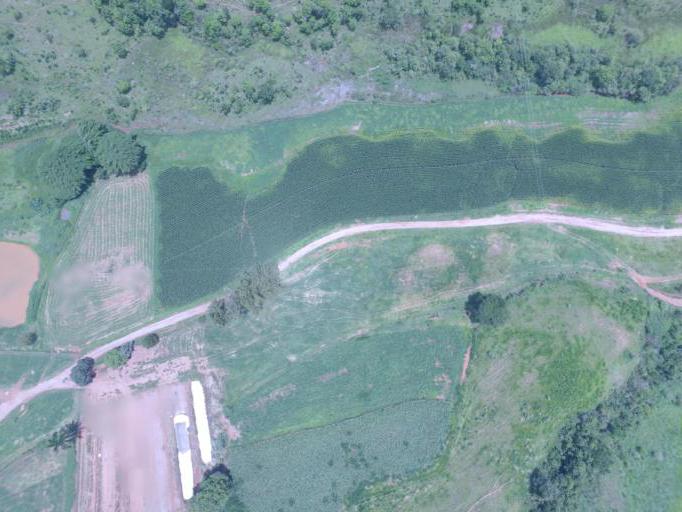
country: BR
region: Minas Gerais
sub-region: Tiradentes
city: Tiradentes
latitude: -21.0834
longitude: -44.0785
